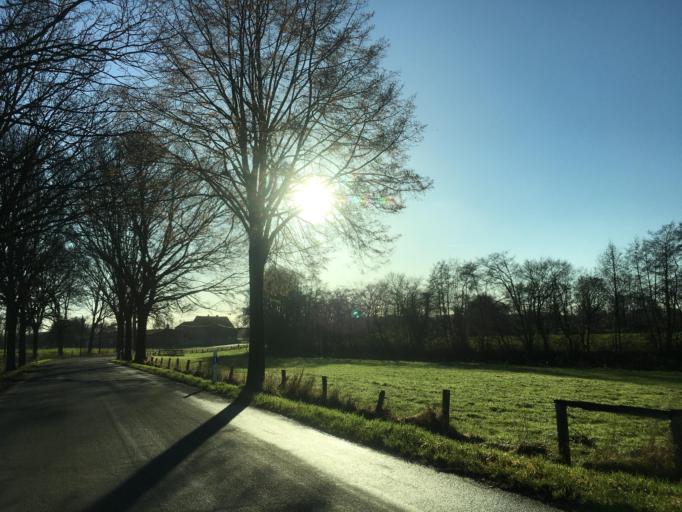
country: DE
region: North Rhine-Westphalia
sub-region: Regierungsbezirk Munster
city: Dulmen
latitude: 51.8587
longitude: 7.2941
